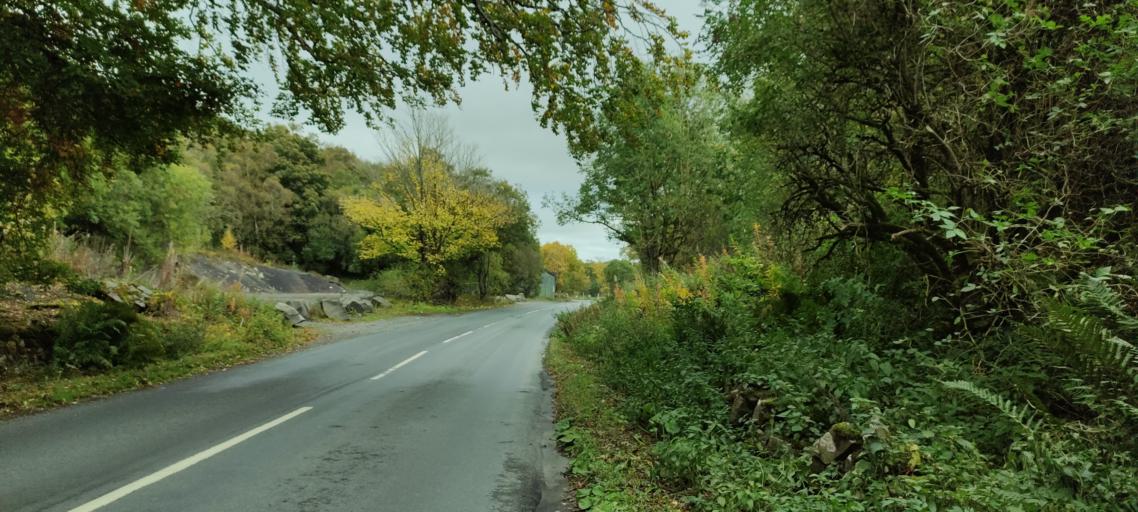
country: GB
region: England
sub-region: County Durham
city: Holwick
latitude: 54.6557
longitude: -2.1896
